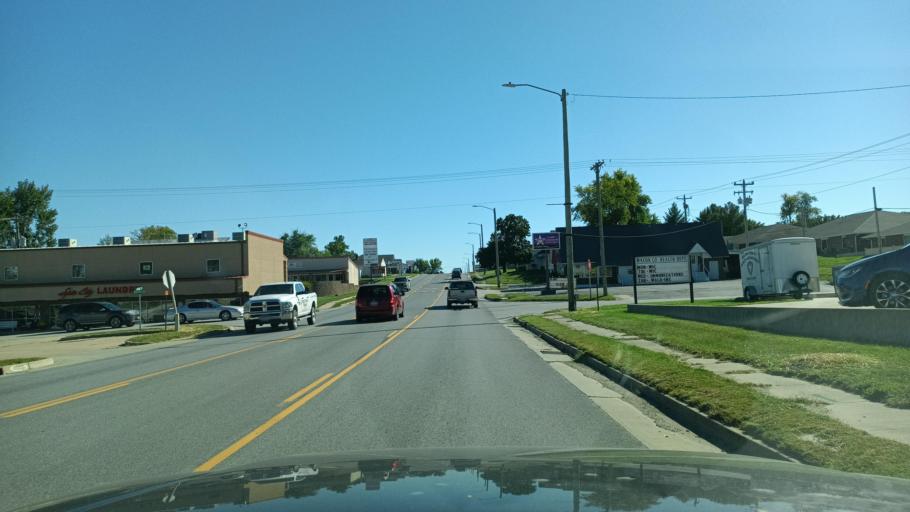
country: US
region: Missouri
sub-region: Macon County
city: Macon
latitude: 39.7428
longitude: -92.4652
